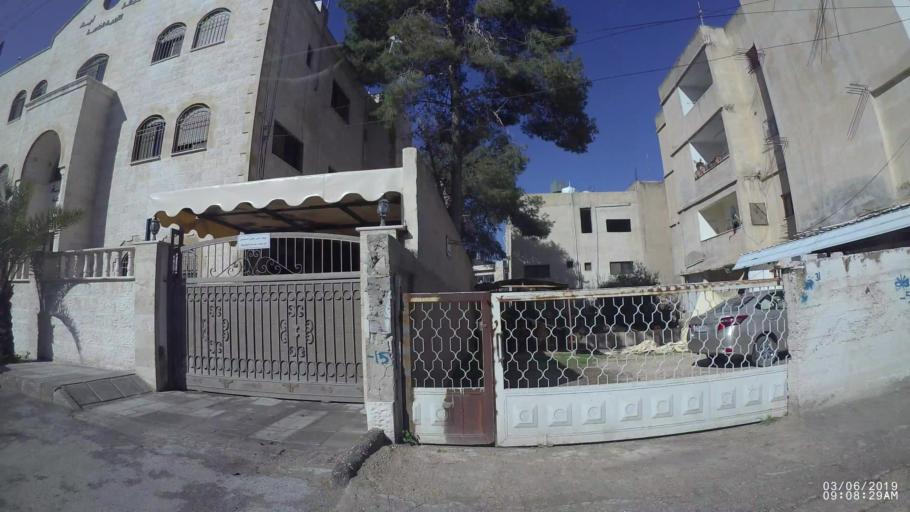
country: JO
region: Amman
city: Amman
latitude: 31.9854
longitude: 35.9894
